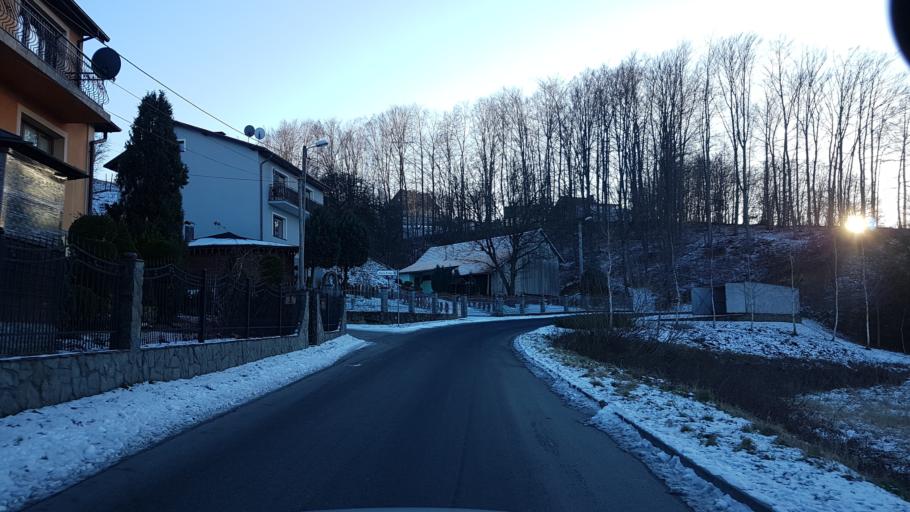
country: PL
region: Lesser Poland Voivodeship
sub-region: Powiat nowosadecki
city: Rytro
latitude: 49.5189
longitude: 20.6633
